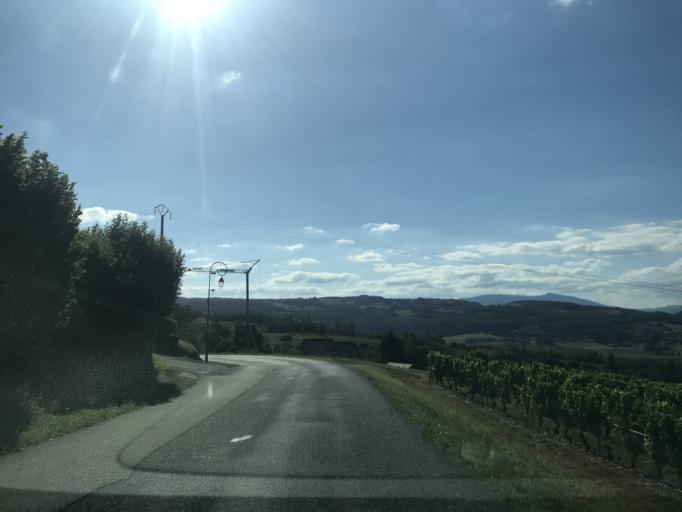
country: FR
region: Rhone-Alpes
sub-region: Departement de la Savoie
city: Yenne
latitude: 45.7339
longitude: 5.8013
